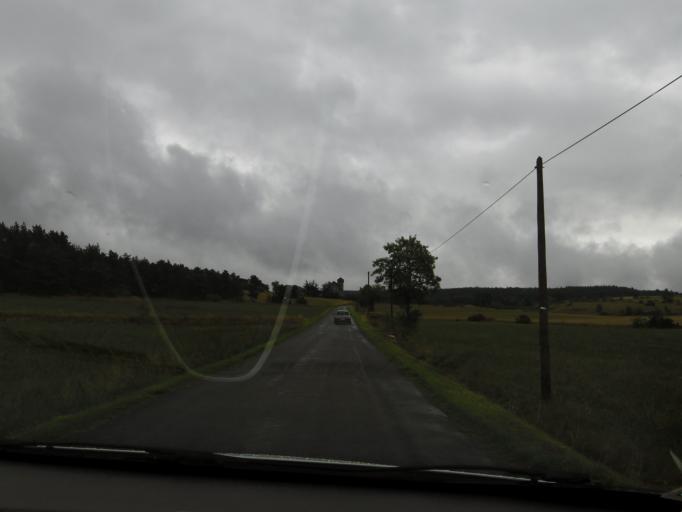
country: FR
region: Languedoc-Roussillon
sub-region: Departement de la Lozere
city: Mende
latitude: 44.4613
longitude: 3.4455
